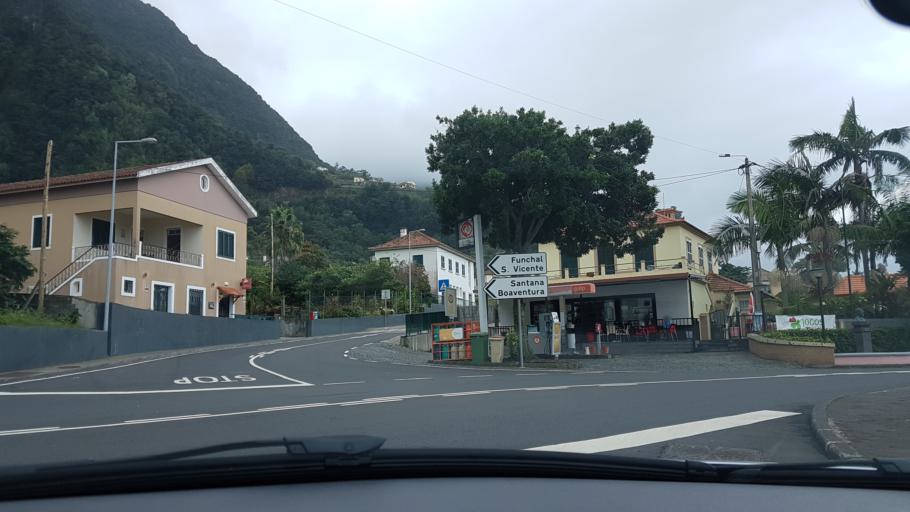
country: PT
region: Madeira
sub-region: Sao Vicente
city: Sao Vicente
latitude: 32.8230
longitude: -16.9896
